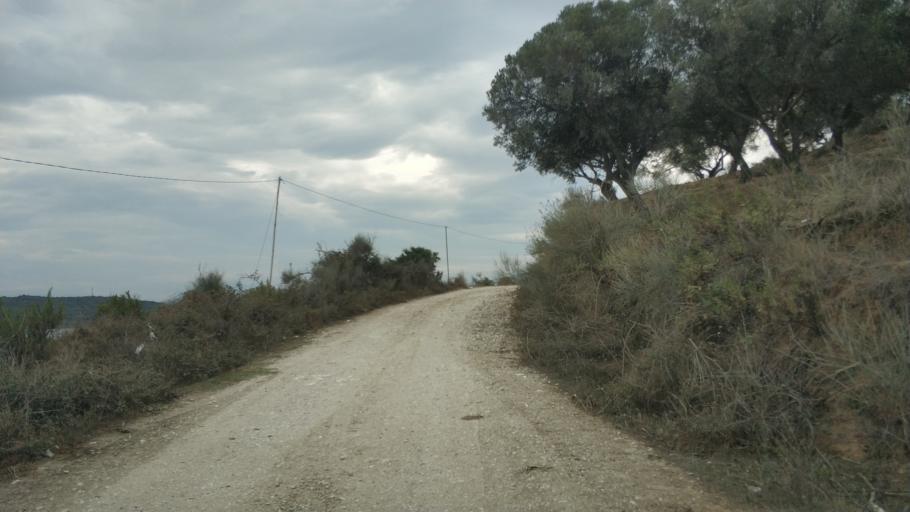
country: AL
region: Vlore
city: Vlore
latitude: 40.5170
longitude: 19.3936
